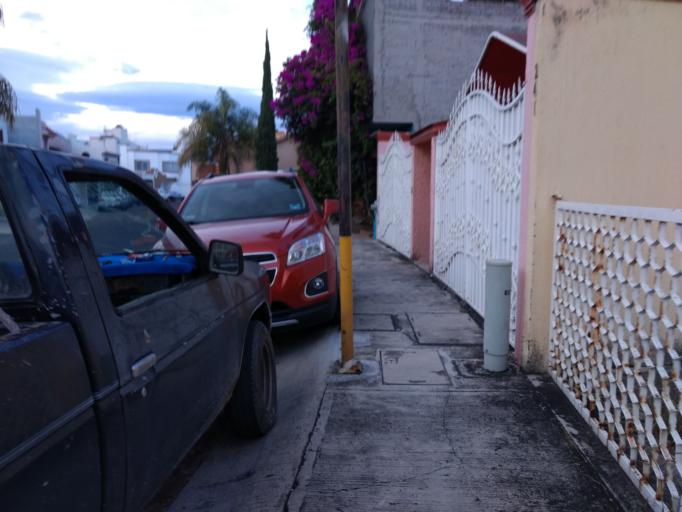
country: MX
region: Michoacan
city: Morelia
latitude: 19.6875
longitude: -101.2184
